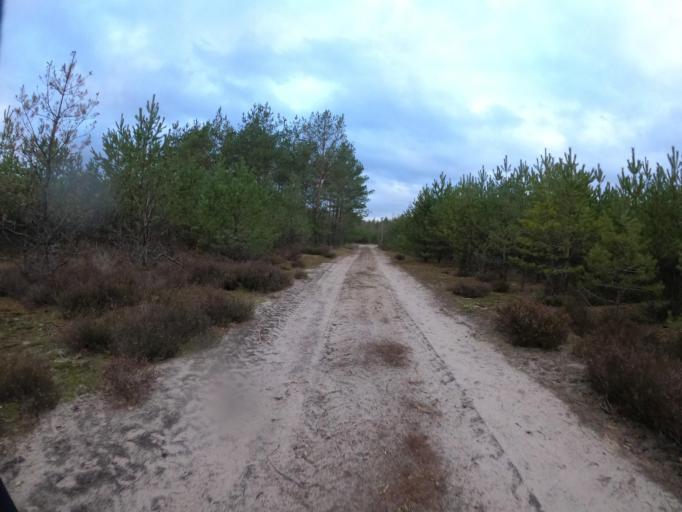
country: PL
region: West Pomeranian Voivodeship
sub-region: Powiat szczecinecki
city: Borne Sulinowo
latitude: 53.5715
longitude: 16.5579
